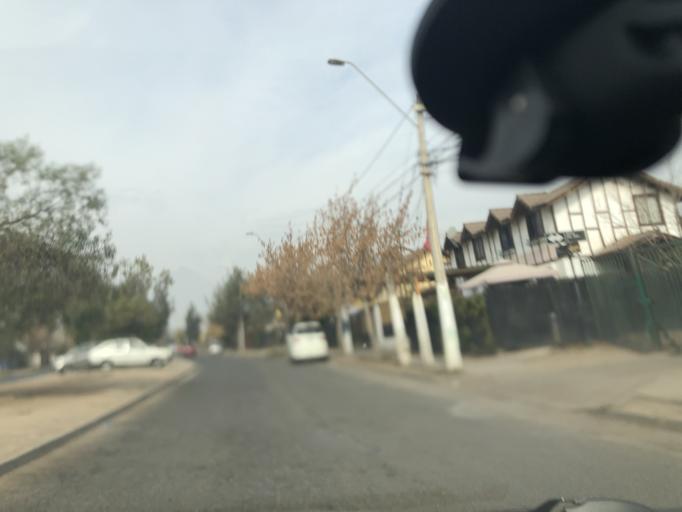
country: CL
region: Santiago Metropolitan
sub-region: Provincia de Cordillera
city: Puente Alto
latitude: -33.5840
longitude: -70.5656
